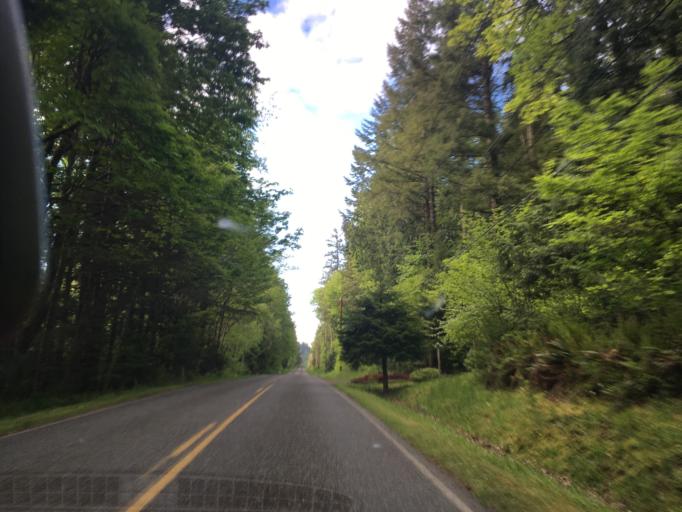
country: US
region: Washington
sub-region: Whatcom County
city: Sudden Valley
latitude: 48.7645
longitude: -122.3553
